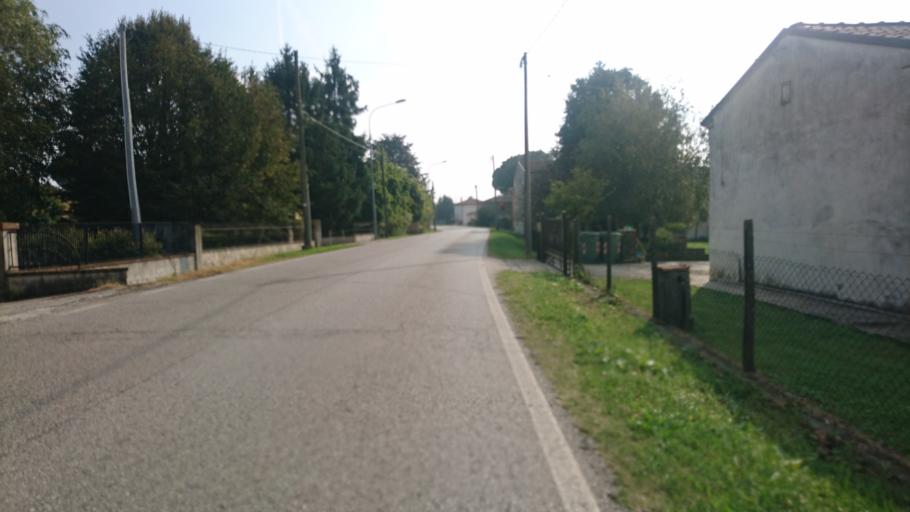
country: IT
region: Veneto
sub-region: Provincia di Rovigo
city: Grignano Polesine
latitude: 45.0371
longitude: 11.7524
